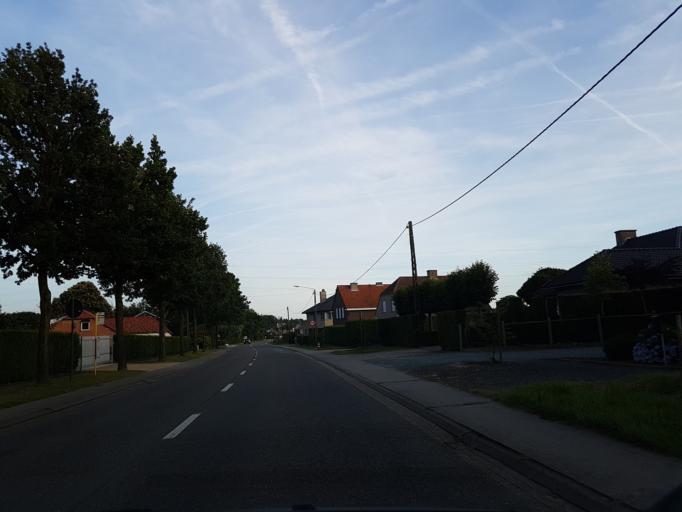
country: BE
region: Flanders
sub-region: Provincie Vlaams-Brabant
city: Merchtem
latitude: 50.9744
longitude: 4.2312
